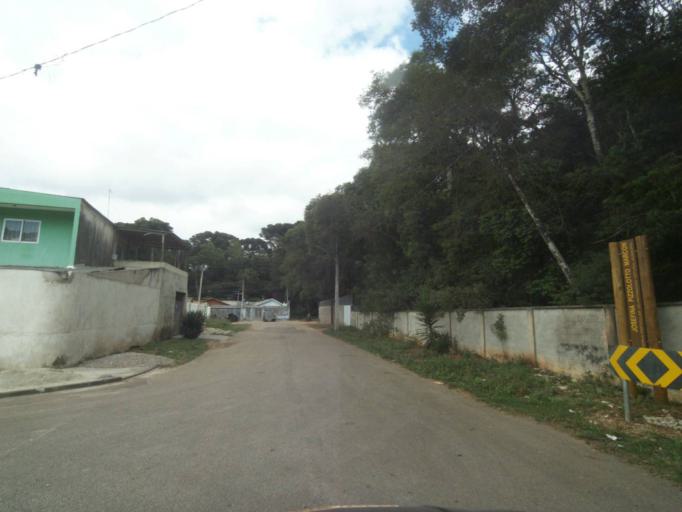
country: BR
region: Parana
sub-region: Sao Jose Dos Pinhais
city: Sao Jose dos Pinhais
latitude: -25.5559
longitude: -49.2602
